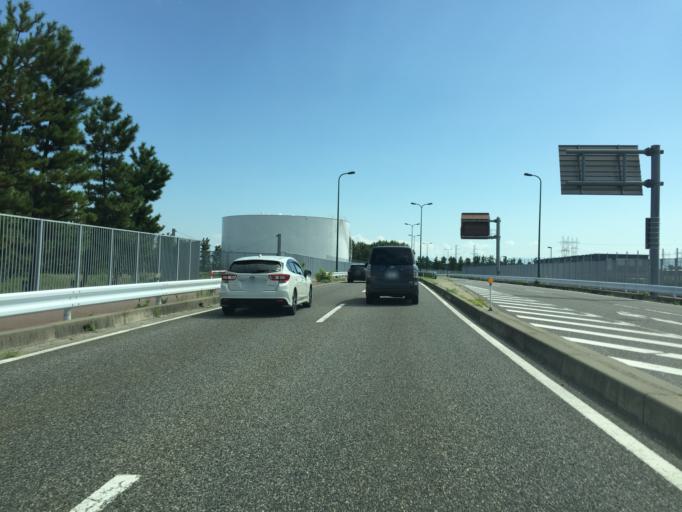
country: JP
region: Niigata
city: Niigata-shi
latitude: 37.9472
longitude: 139.0827
